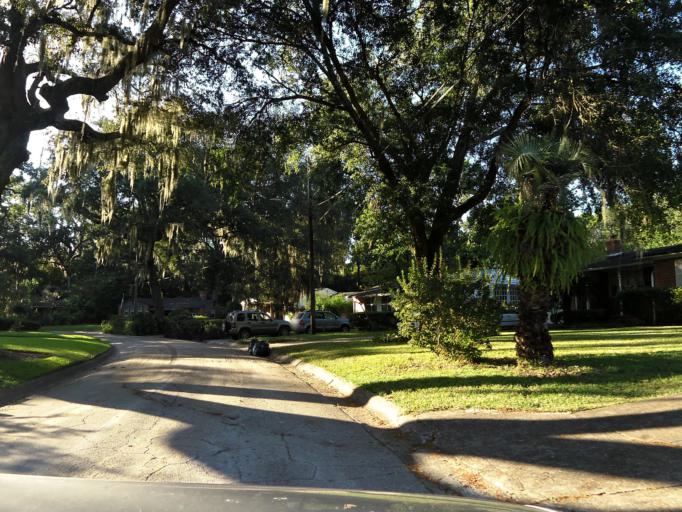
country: US
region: Florida
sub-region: Duval County
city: Jacksonville
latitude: 30.2692
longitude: -81.6405
